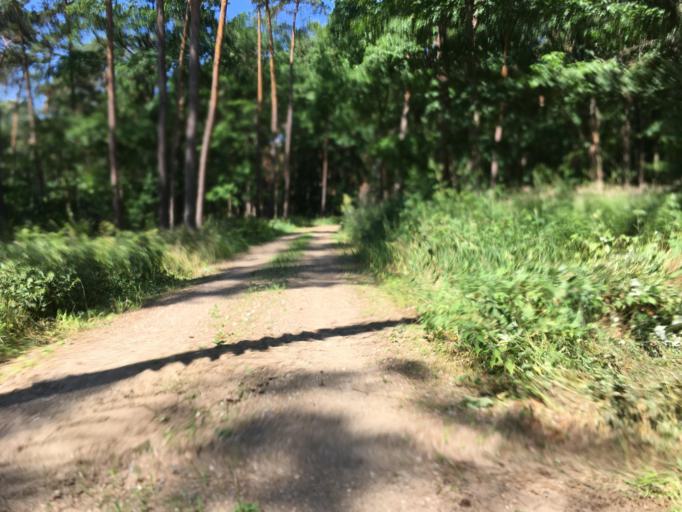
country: DE
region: Brandenburg
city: Marienwerder
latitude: 52.9227
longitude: 13.6165
